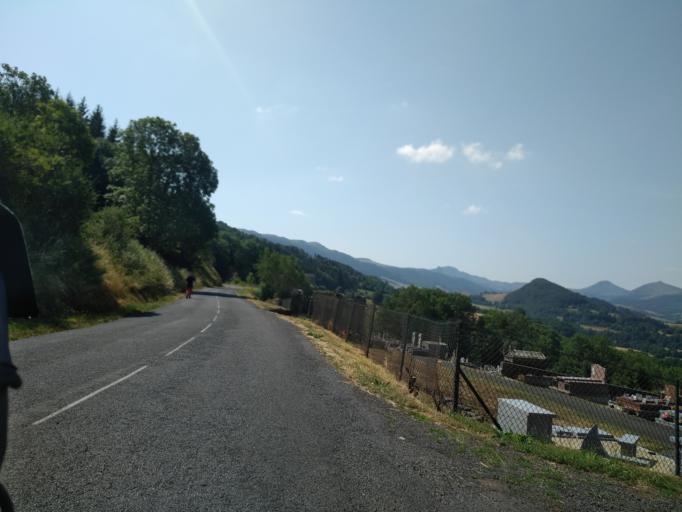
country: FR
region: Auvergne
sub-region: Departement du Cantal
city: Riom-es-Montagnes
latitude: 45.2040
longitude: 2.7157
